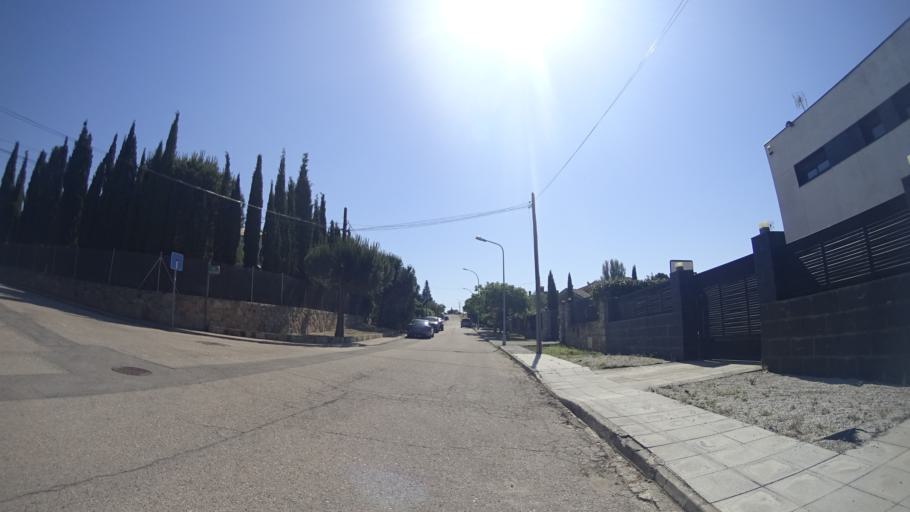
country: ES
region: Madrid
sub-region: Provincia de Madrid
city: Hoyo de Manzanares
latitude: 40.6035
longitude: -3.9032
